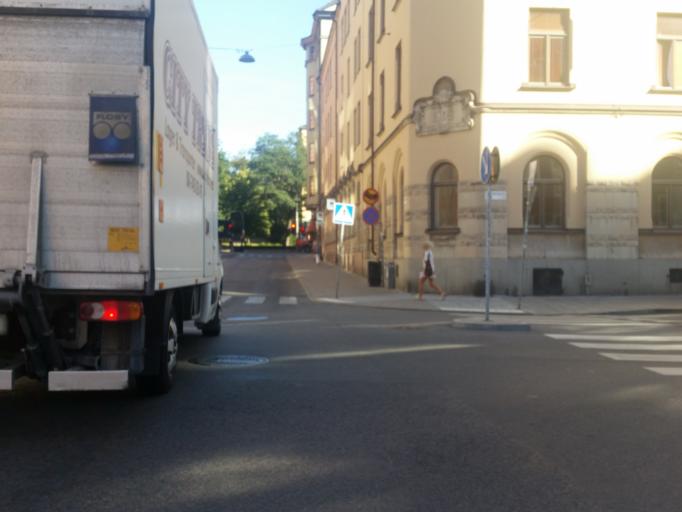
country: SE
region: Stockholm
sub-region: Stockholms Kommun
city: Stockholm
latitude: 59.3172
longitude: 18.0556
